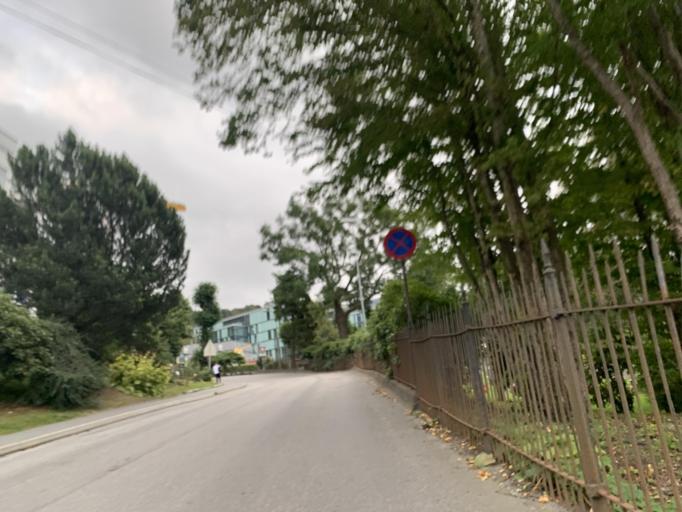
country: NO
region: Hordaland
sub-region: Bergen
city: Bergen
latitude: 60.3773
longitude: 5.3574
